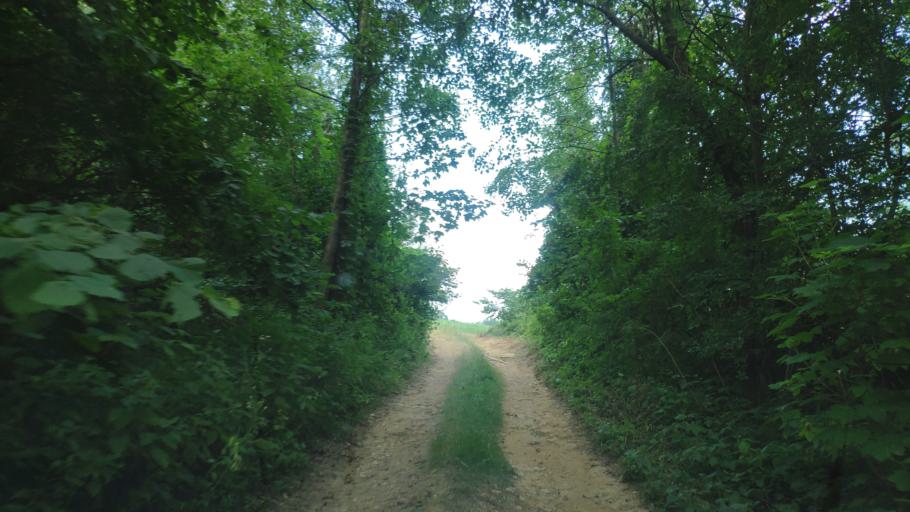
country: SK
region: Kosicky
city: Medzev
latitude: 48.7064
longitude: 20.9858
